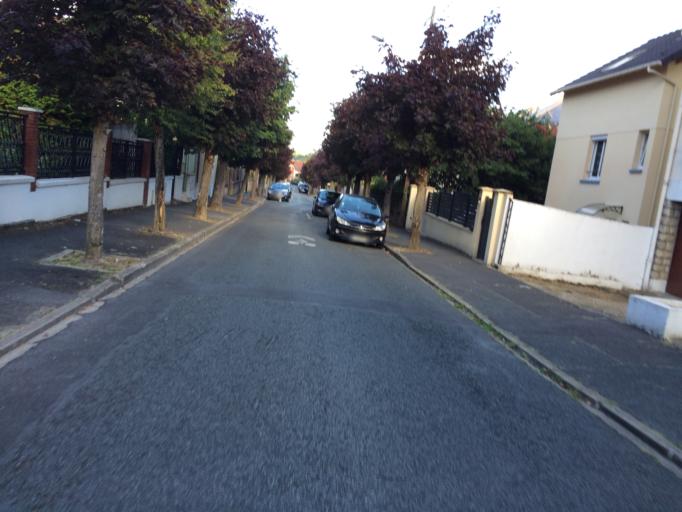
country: FR
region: Ile-de-France
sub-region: Departement de l'Essonne
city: Orsay
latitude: 48.7051
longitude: 2.2120
